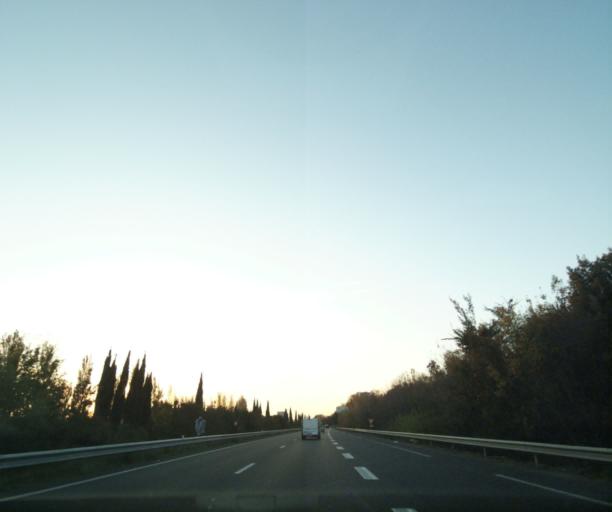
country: FR
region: Provence-Alpes-Cote d'Azur
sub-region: Departement des Bouches-du-Rhone
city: Saint-Martin-de-Crau
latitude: 43.6380
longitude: 4.8529
